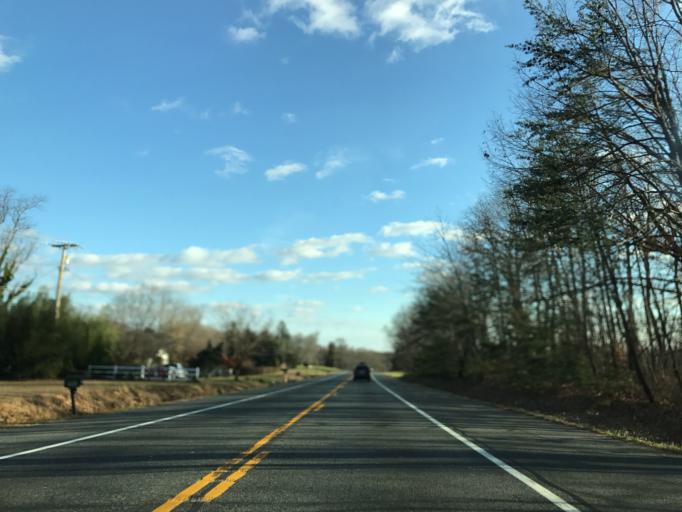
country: US
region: Maryland
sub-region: Harford County
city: Joppatowne
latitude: 39.4566
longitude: -76.3592
